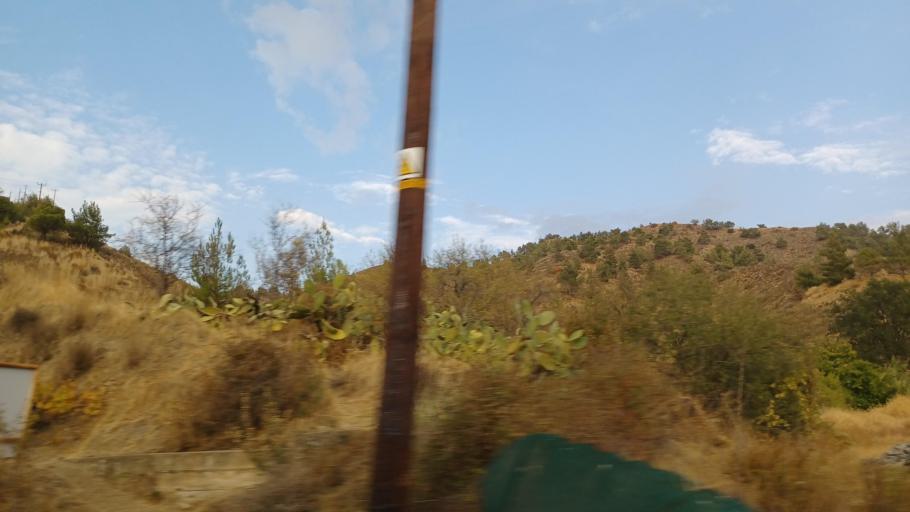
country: CY
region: Lefkosia
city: Kakopetria
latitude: 35.0002
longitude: 32.8994
